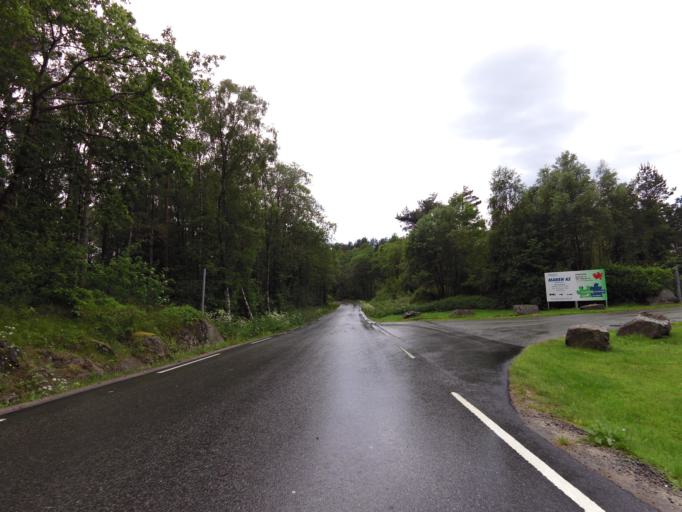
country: NO
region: Vest-Agder
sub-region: Mandal
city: Mandal
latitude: 58.0165
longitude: 7.5126
